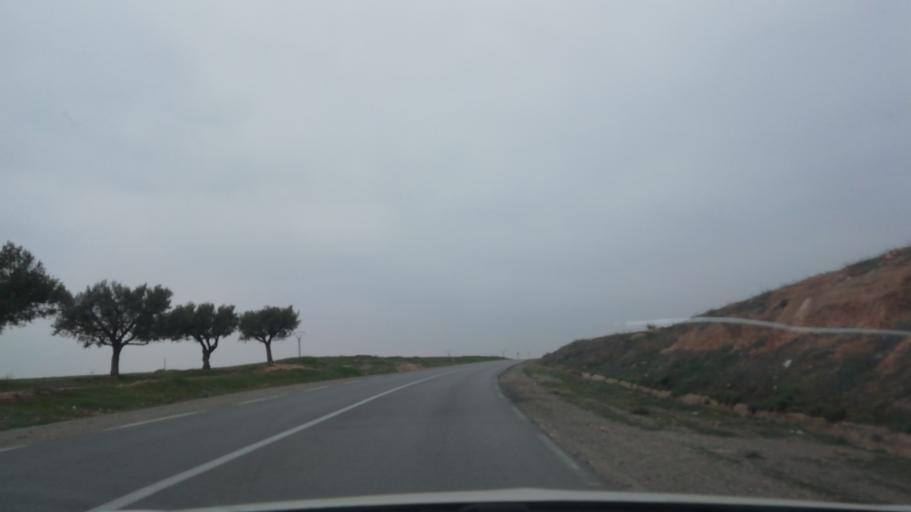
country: DZ
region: Sidi Bel Abbes
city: Sfizef
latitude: 35.2720
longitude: -0.1564
